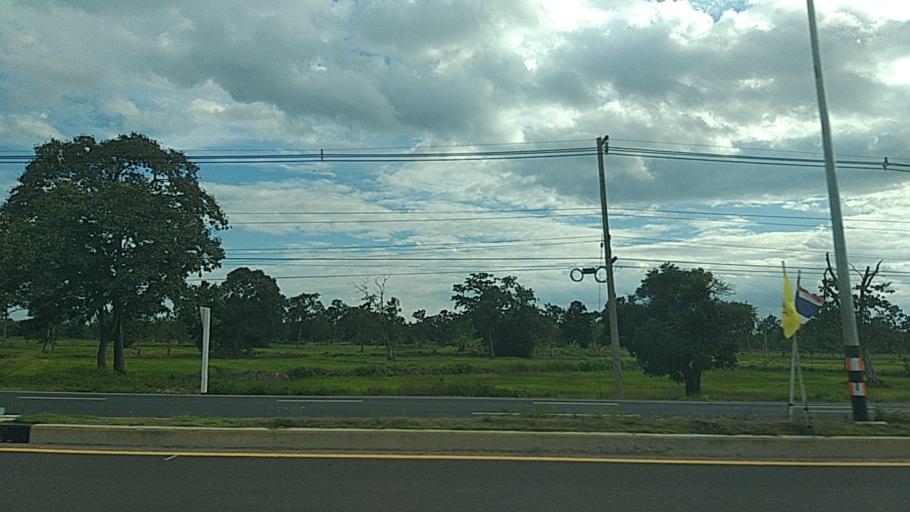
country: TH
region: Surin
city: Prasat
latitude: 14.5604
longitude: 103.4992
